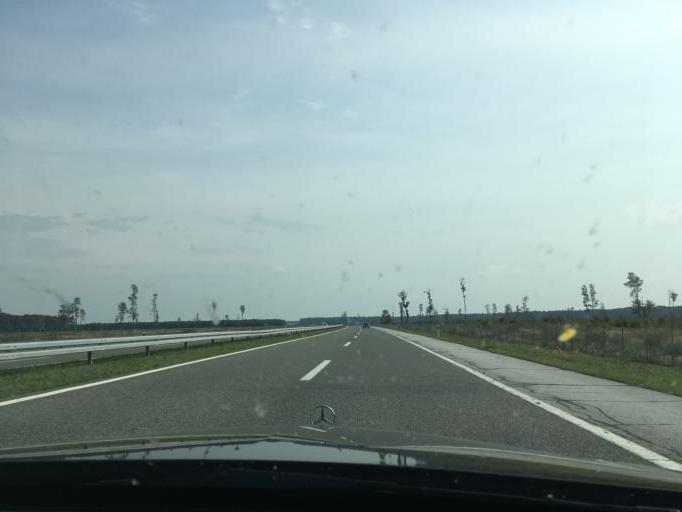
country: HR
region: Vukovarsko-Srijemska
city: Vrbanja
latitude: 45.0457
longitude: 18.8580
